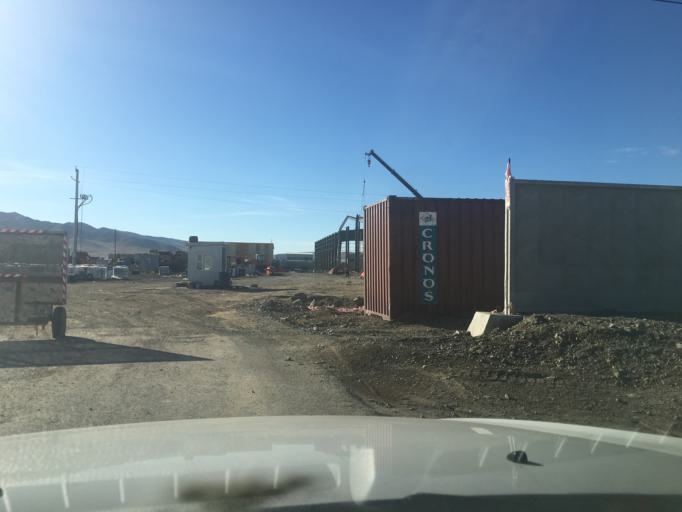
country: MN
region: Ulaanbaatar
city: Ulaanbaatar
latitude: 47.8969
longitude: 106.7038
